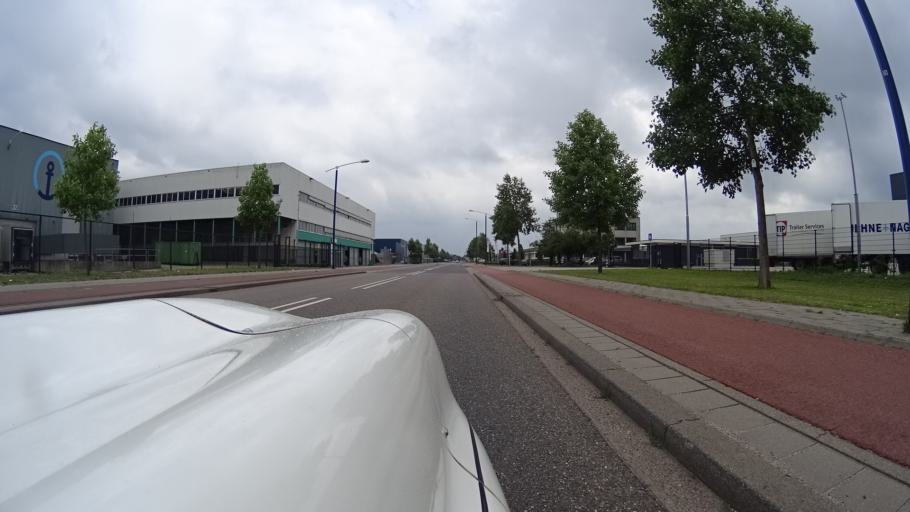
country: NL
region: North Brabant
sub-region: Gemeente Veghel
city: Eerde
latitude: 51.6087
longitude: 5.5187
